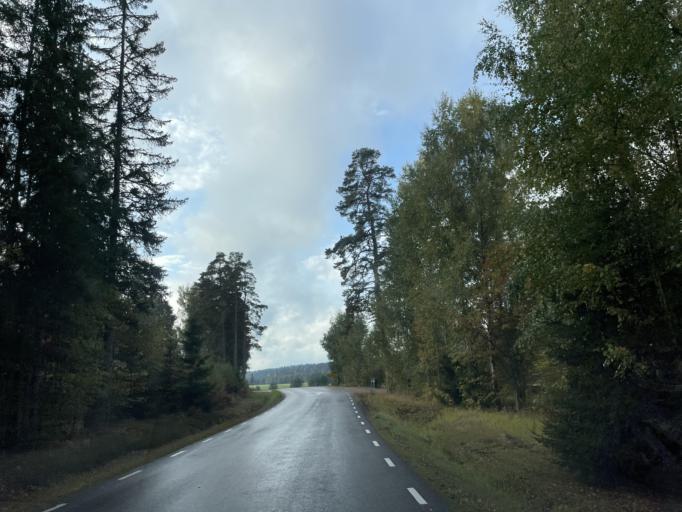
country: SE
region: Vaermland
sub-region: Karlstads Kommun
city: Skattkarr
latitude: 59.4306
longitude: 13.6060
